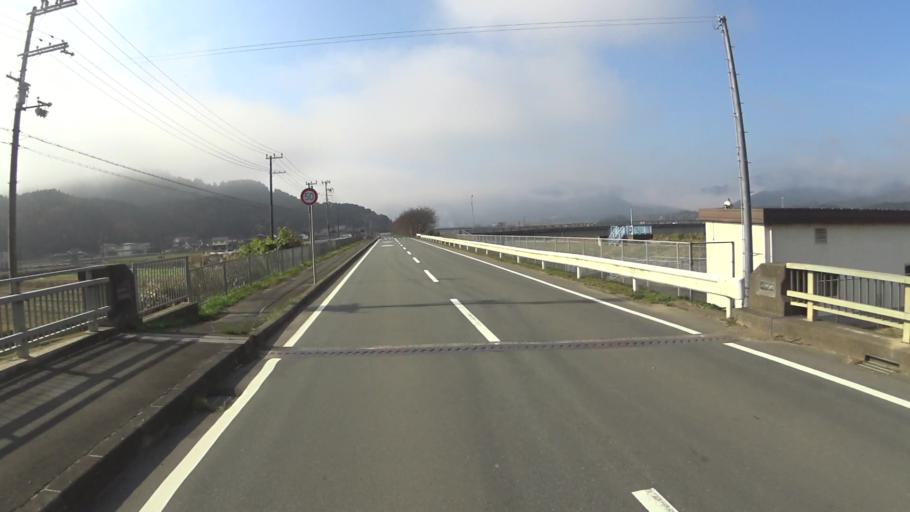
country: JP
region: Kyoto
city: Fukuchiyama
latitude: 35.2484
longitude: 135.1567
